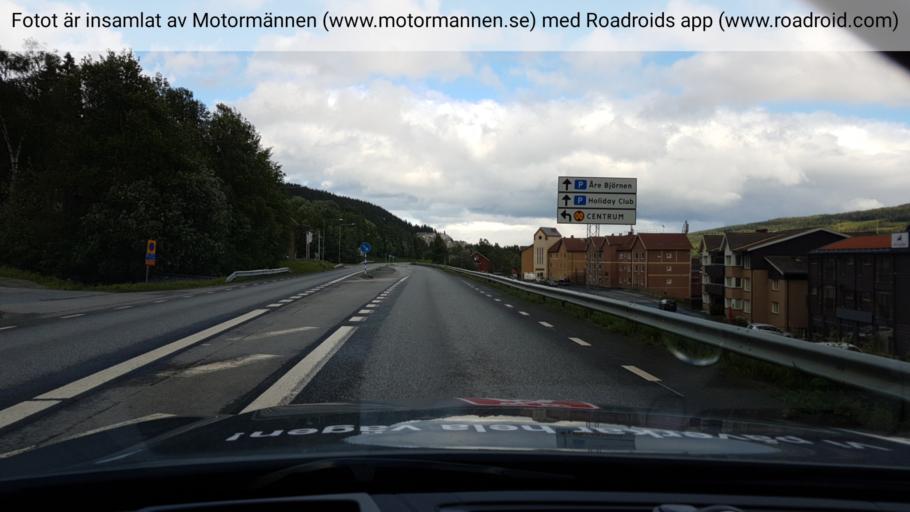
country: SE
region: Jaemtland
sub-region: Are Kommun
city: Are
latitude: 63.4007
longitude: 13.0803
